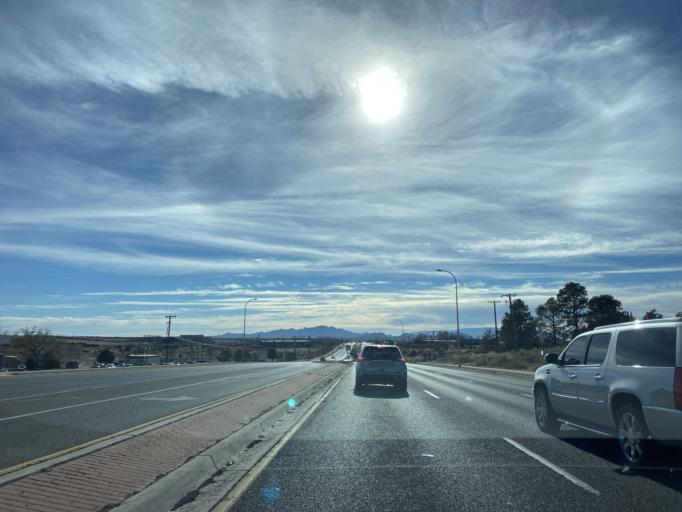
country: US
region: New Mexico
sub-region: Santa Fe County
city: Agua Fria
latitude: 35.6300
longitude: -106.0230
